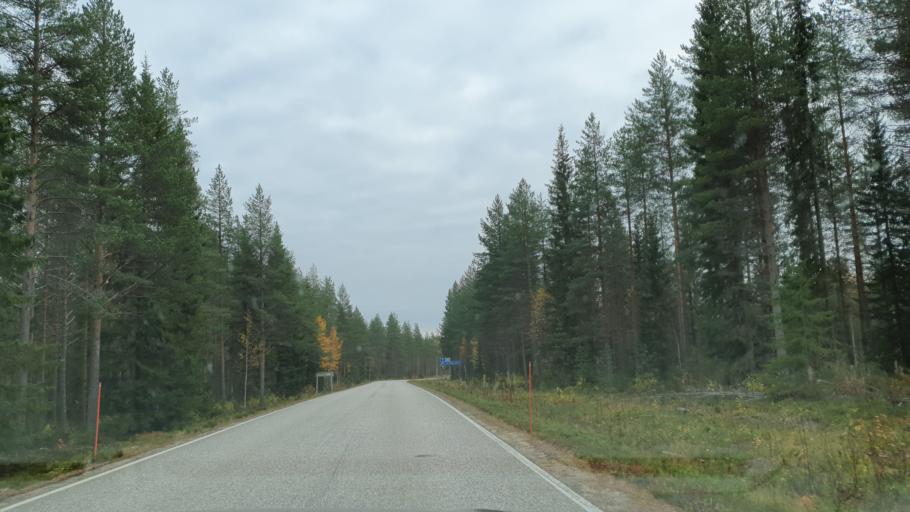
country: FI
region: Kainuu
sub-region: Kajaani
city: Ristijaervi
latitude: 64.4635
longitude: 28.3126
